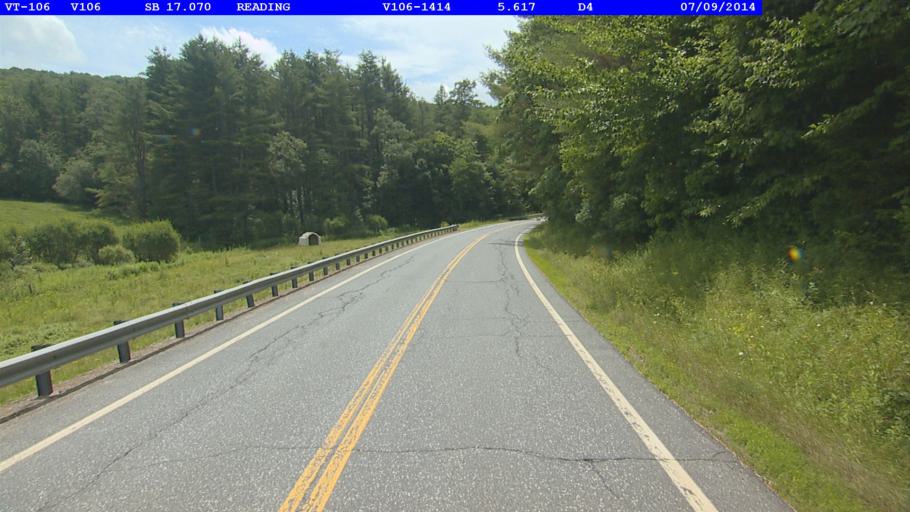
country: US
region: Vermont
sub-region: Windsor County
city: Woodstock
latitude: 43.5162
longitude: -72.5484
